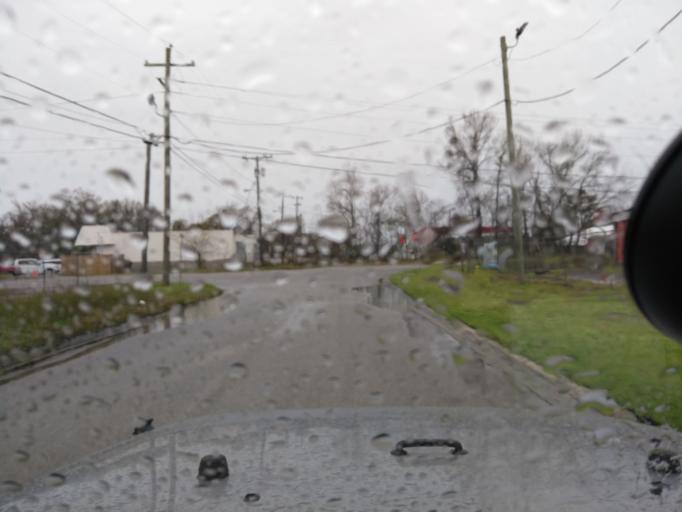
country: US
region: Georgia
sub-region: Chatham County
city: Garden City
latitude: 32.0875
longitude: -81.1602
